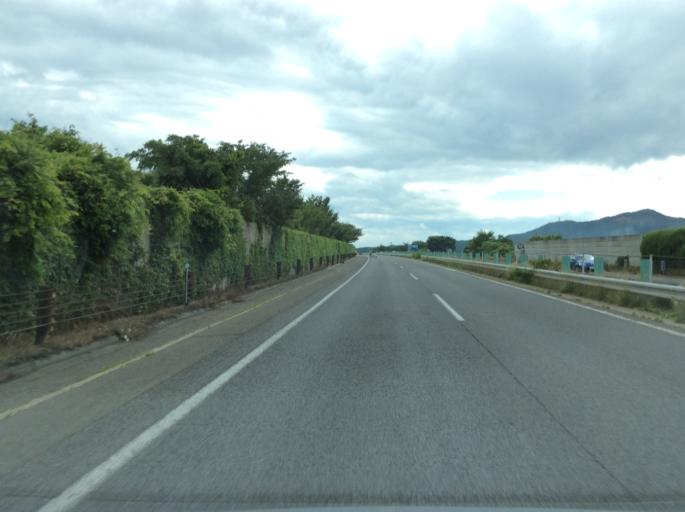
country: JP
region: Fukushima
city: Motomiya
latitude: 37.5436
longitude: 140.3891
